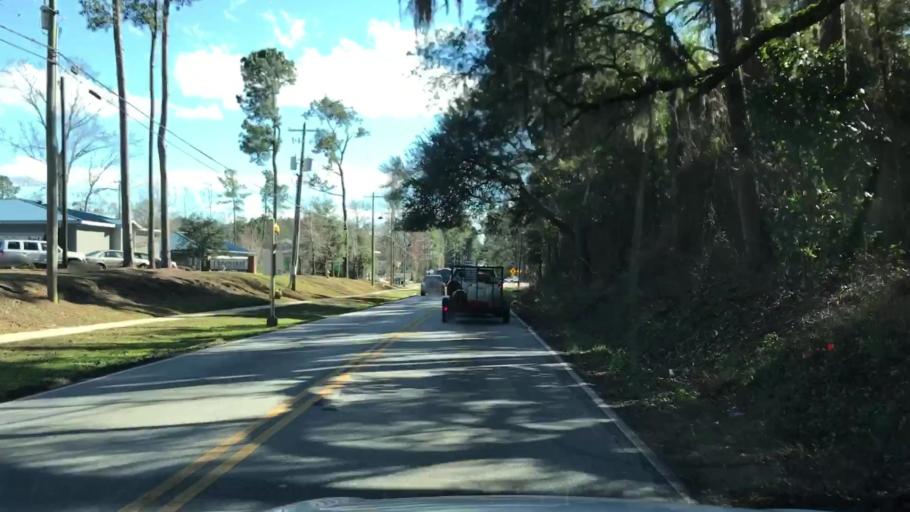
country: US
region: South Carolina
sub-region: Dorchester County
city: Summerville
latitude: 33.0240
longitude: -80.2424
